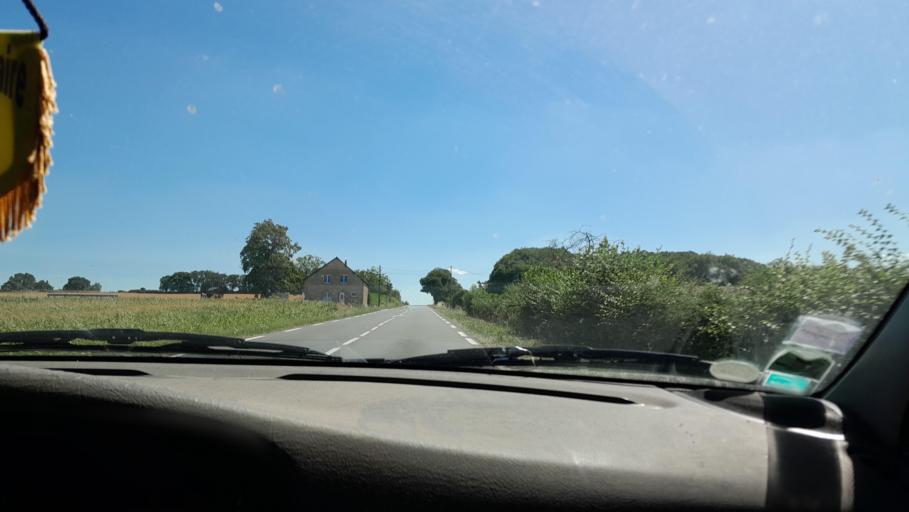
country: FR
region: Pays de la Loire
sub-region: Departement de la Loire-Atlantique
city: Saint-Mars-la-Jaille
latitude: 47.5481
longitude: -1.1853
